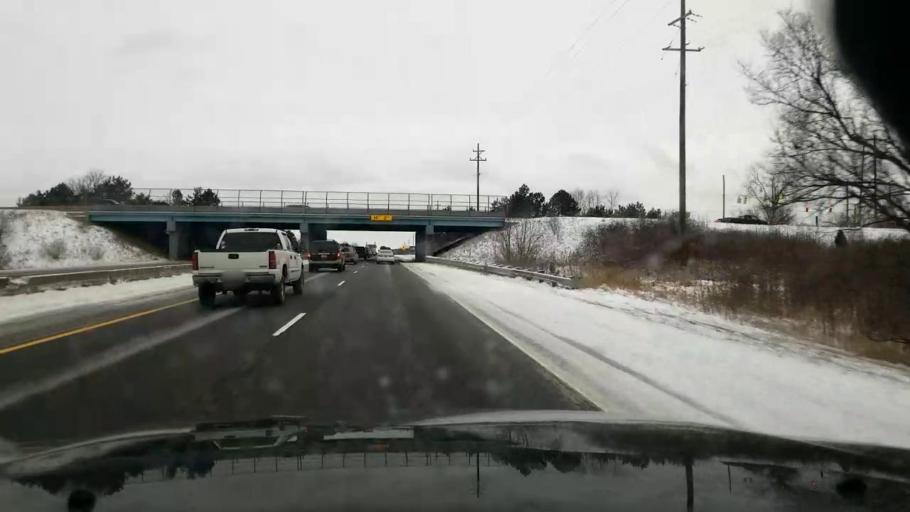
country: US
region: Michigan
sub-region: Jackson County
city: Jackson
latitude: 42.2691
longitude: -84.4514
